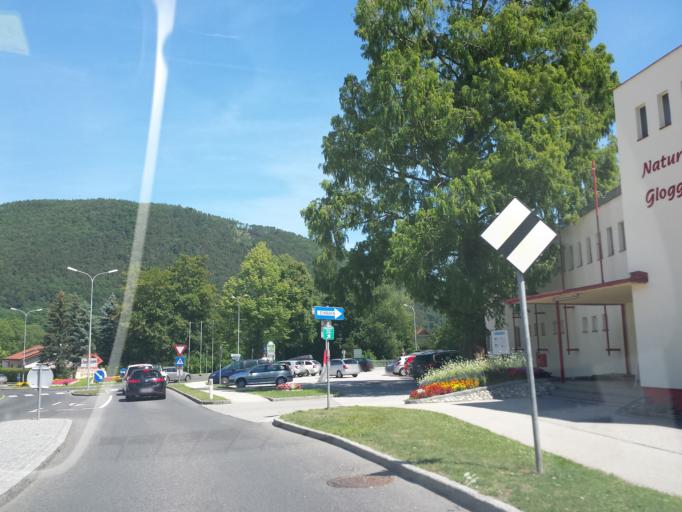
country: AT
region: Lower Austria
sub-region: Politischer Bezirk Neunkirchen
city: Gloggnitz
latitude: 47.6709
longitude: 15.9313
